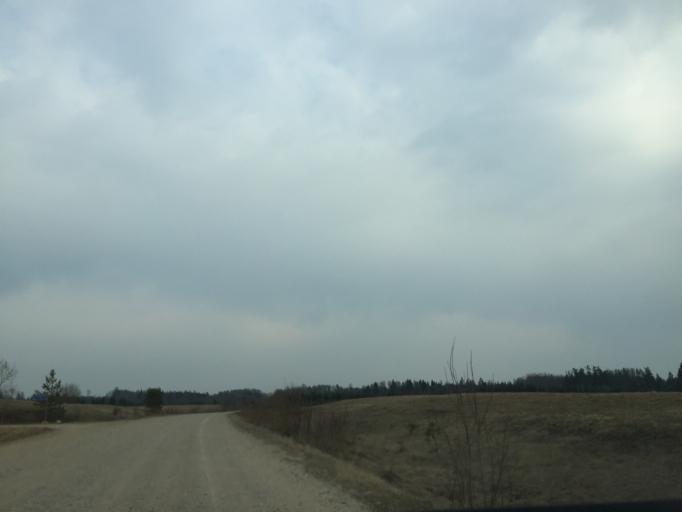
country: LV
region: Priekuli
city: Priekuli
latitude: 57.1889
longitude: 25.4542
